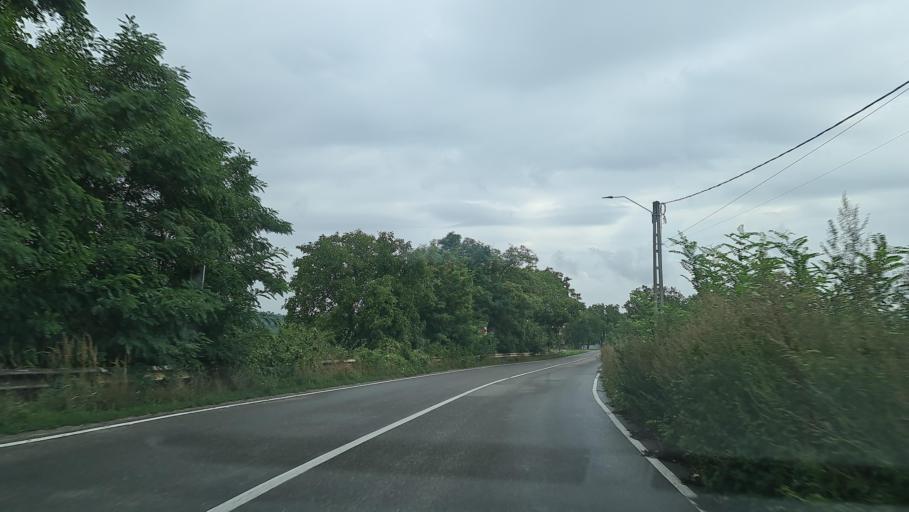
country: RO
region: Neamt
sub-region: Comuna Borlesti
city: Borlesti
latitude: 46.7616
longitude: 26.4662
